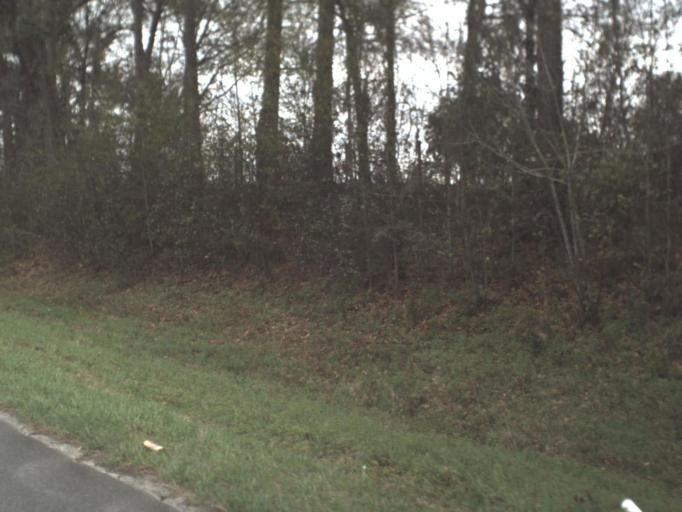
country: US
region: Florida
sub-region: Leon County
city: Tallahassee
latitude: 30.5199
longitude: -84.3499
